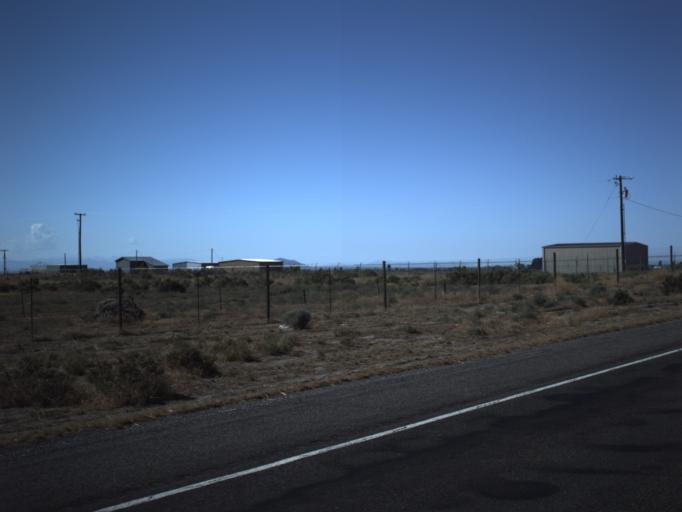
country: US
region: Utah
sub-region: Millard County
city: Delta
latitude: 39.3891
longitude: -112.5139
